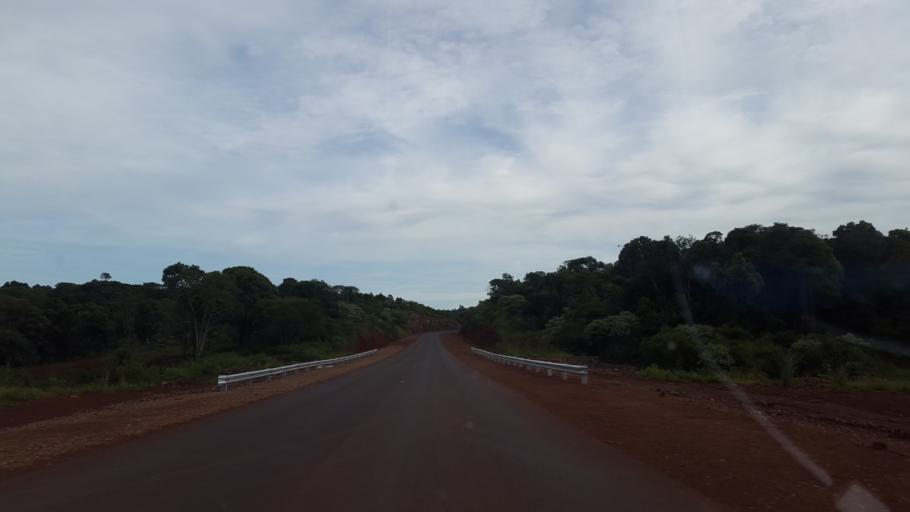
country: AR
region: Misiones
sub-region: Departamento de San Pedro
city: San Pedro
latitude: -26.4691
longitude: -53.8763
